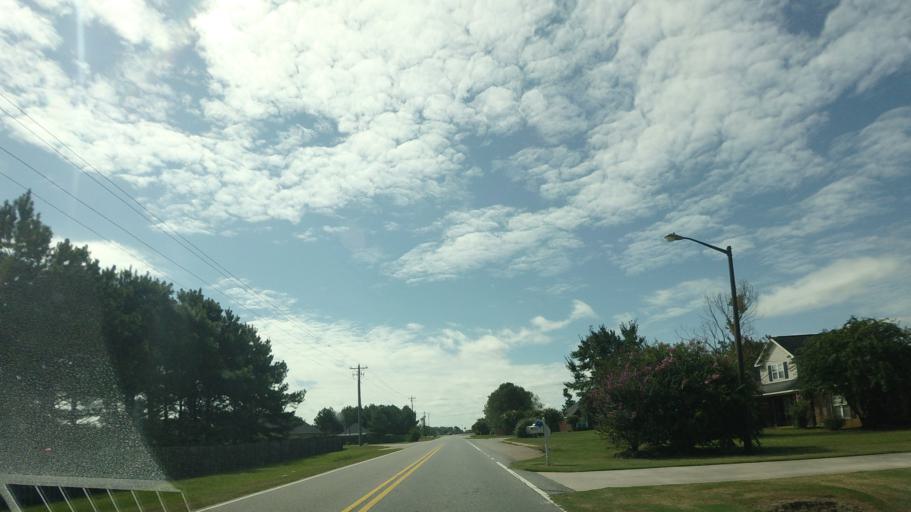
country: US
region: Georgia
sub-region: Houston County
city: Centerville
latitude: 32.5838
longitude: -83.7005
